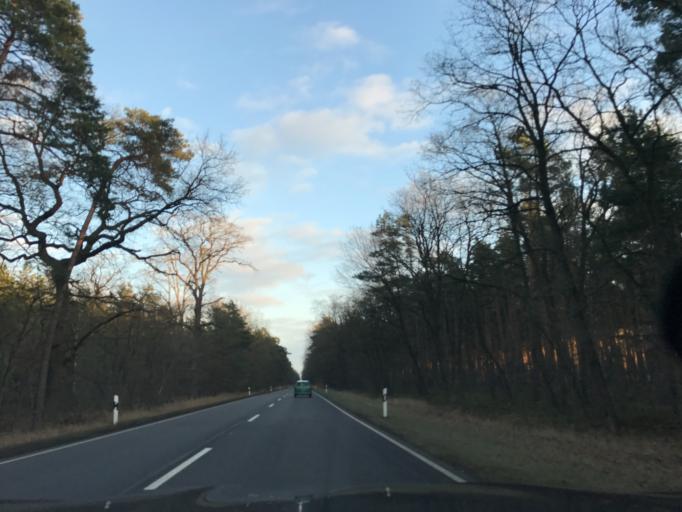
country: DE
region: Brandenburg
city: Bensdorf
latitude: 52.4113
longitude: 12.2624
